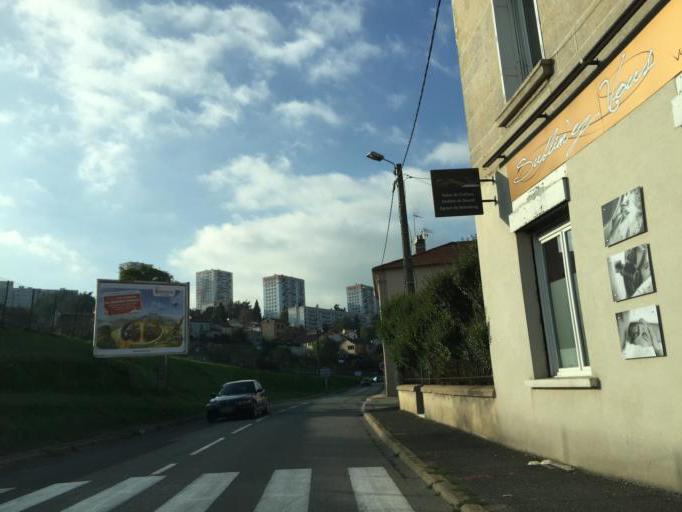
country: FR
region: Rhone-Alpes
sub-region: Departement de la Loire
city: Saint-Priest-en-Jarez
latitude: 45.4660
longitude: 4.3697
